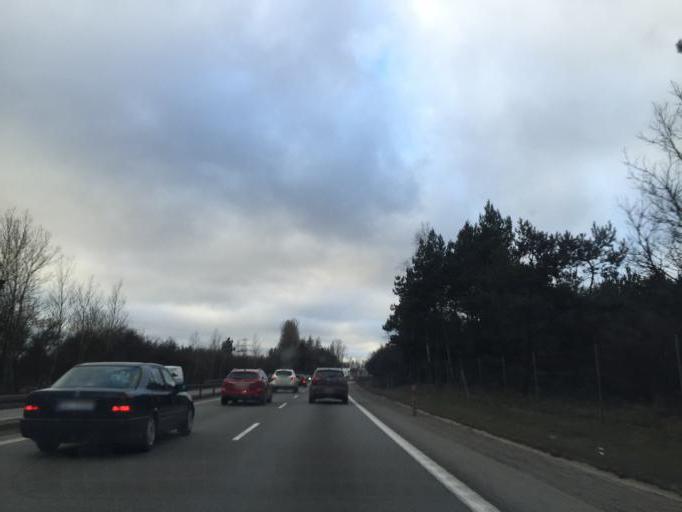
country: PL
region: Pomeranian Voivodeship
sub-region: Gdynia
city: Wielki Kack
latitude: 54.3921
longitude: 18.4912
